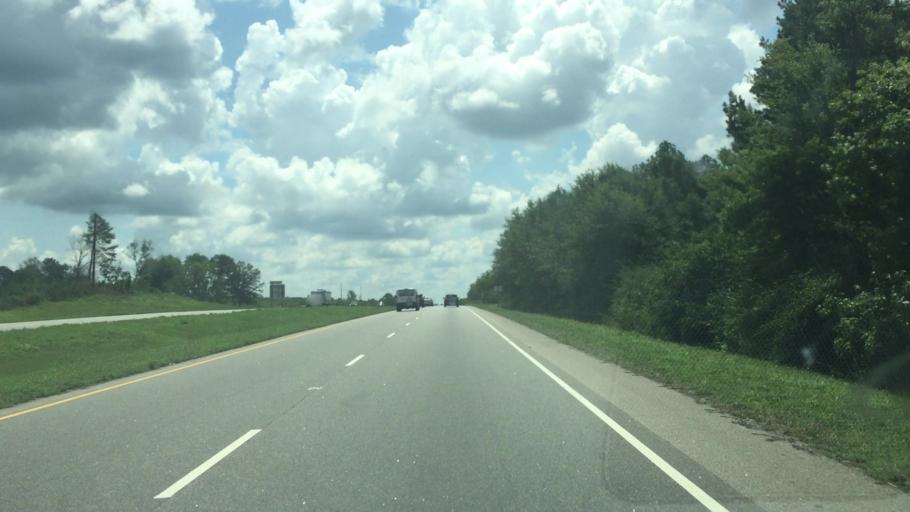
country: US
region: North Carolina
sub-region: Richmond County
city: Hamlet
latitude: 34.8516
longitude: -79.6193
